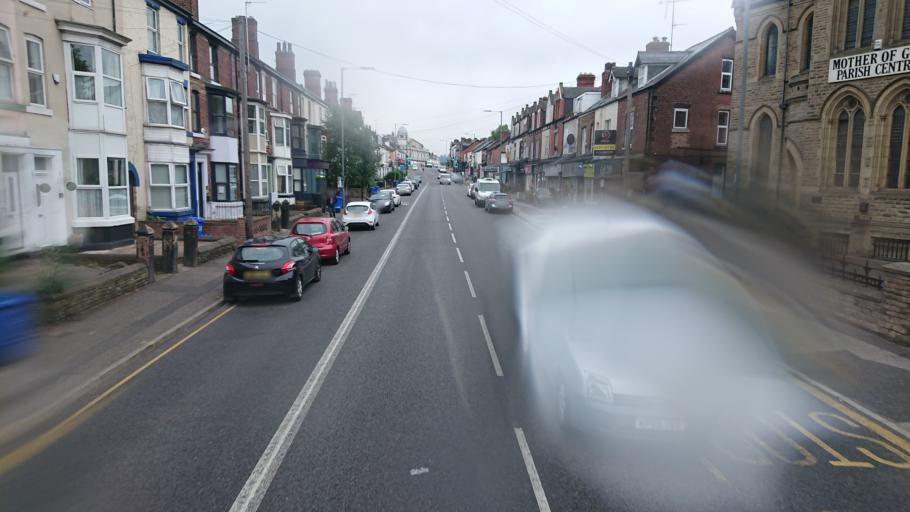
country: GB
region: England
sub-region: Sheffield
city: Sheffield
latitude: 53.3621
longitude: -1.4784
